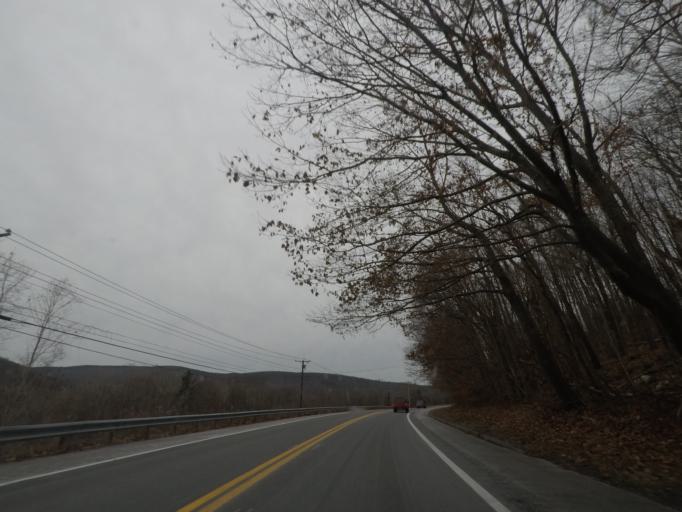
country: US
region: Massachusetts
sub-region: Berkshire County
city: Lanesborough
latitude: 42.5521
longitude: -73.3076
